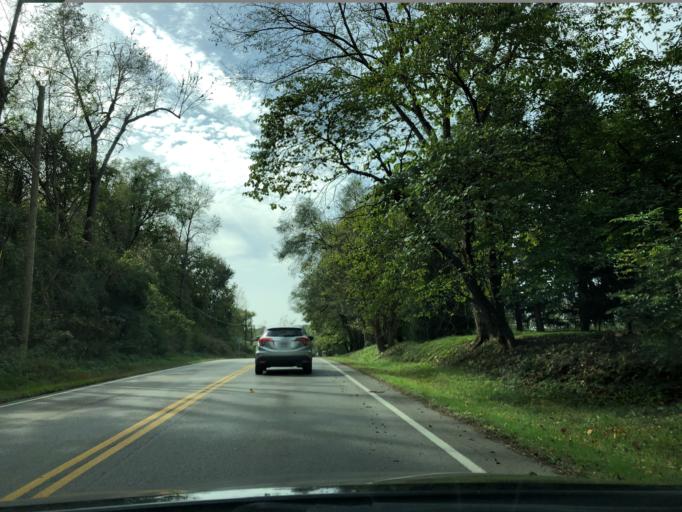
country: US
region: Ohio
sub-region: Clermont County
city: Milford
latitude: 39.1907
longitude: -84.2903
